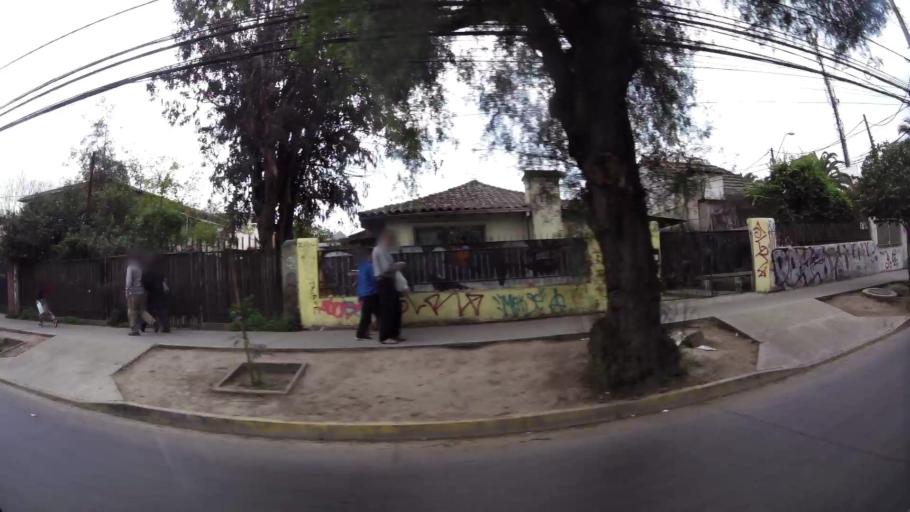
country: CL
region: Santiago Metropolitan
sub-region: Provincia de Santiago
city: Lo Prado
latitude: -33.5104
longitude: -70.7524
